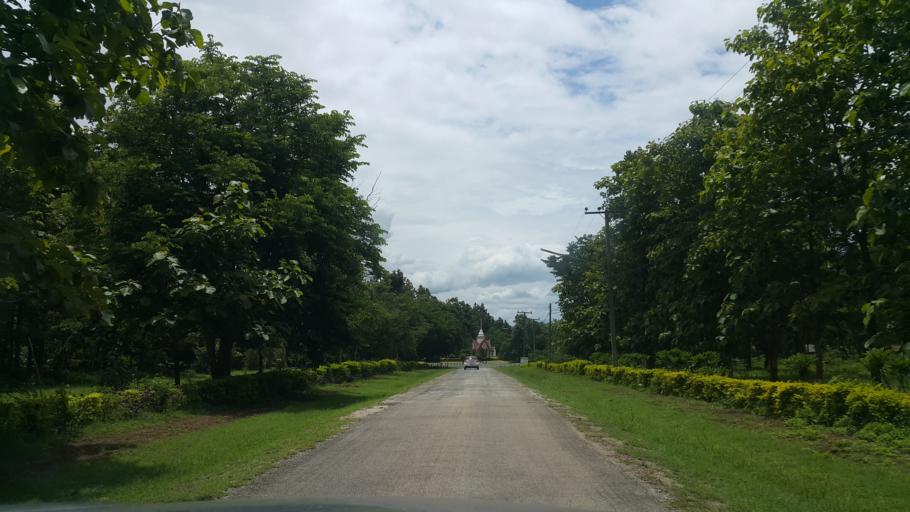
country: TH
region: Chiang Mai
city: Mae Taeng
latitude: 19.1829
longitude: 98.9655
